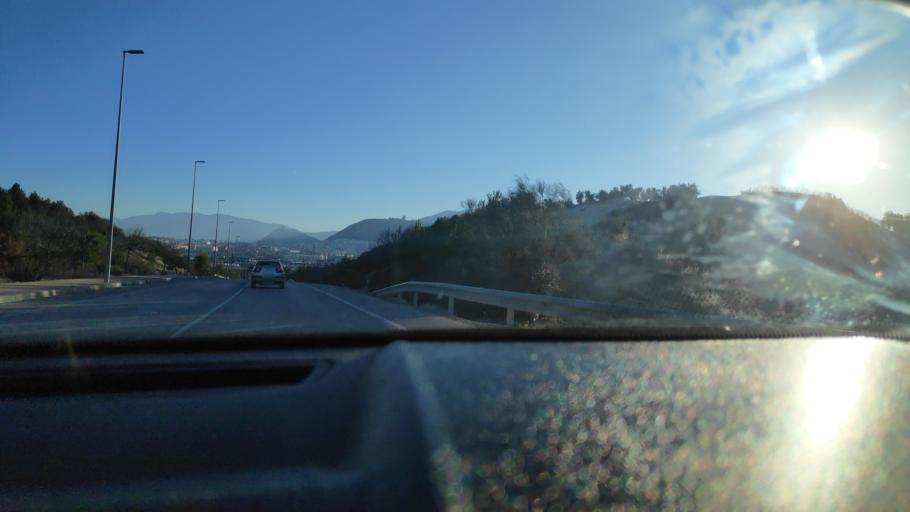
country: ES
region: Andalusia
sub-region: Provincia de Jaen
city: Jaen
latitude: 37.8064
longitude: -3.7880
